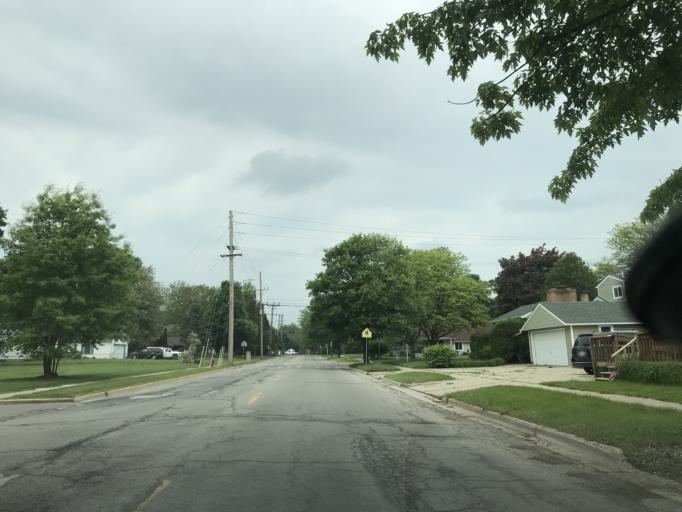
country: US
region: Michigan
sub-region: Livingston County
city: Brighton
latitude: 42.5268
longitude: -83.7923
